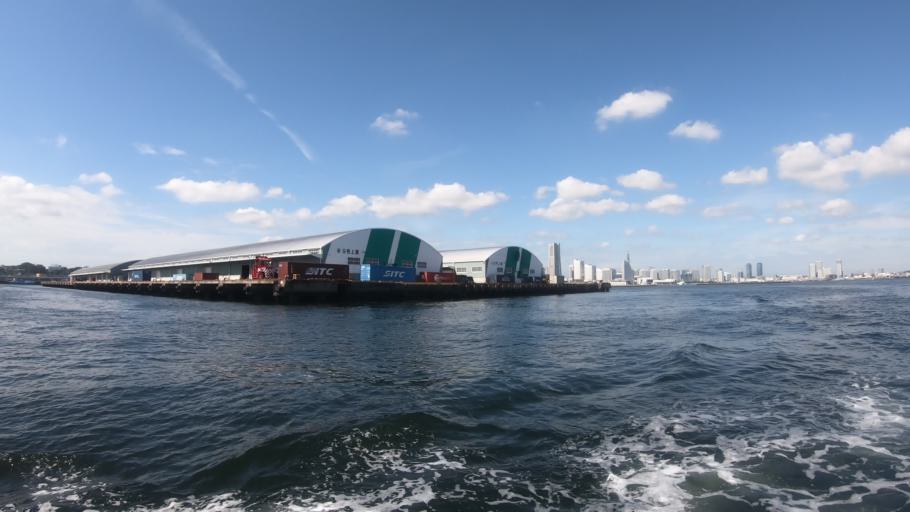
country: JP
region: Kanagawa
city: Yokohama
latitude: 35.4498
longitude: 139.6664
